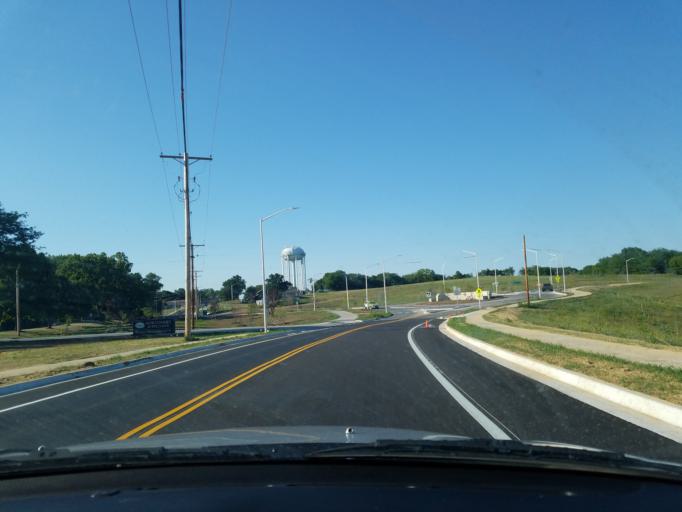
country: US
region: Missouri
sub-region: Clay County
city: Gladstone
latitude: 39.2127
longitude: -94.5353
